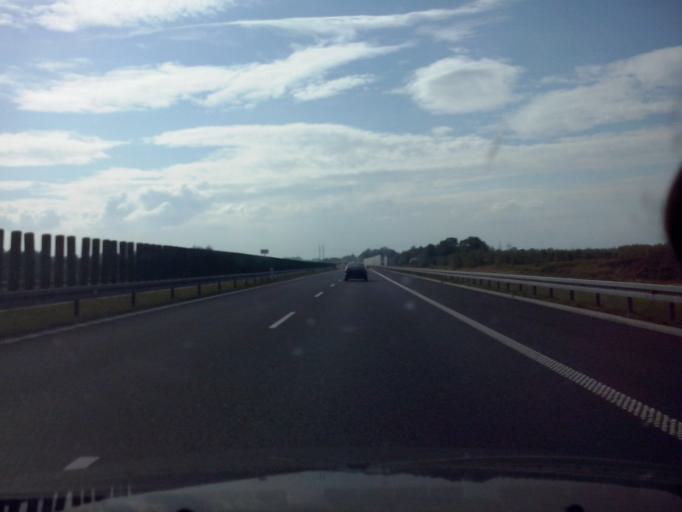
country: PL
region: Lesser Poland Voivodeship
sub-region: Powiat tarnowski
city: Lukowa
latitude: 50.0583
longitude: 20.9367
